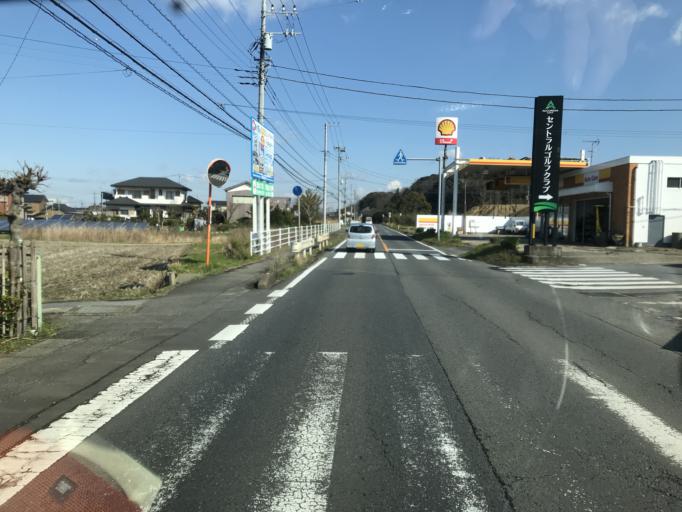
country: JP
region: Ibaraki
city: Itako
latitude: 36.0000
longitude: 140.4721
